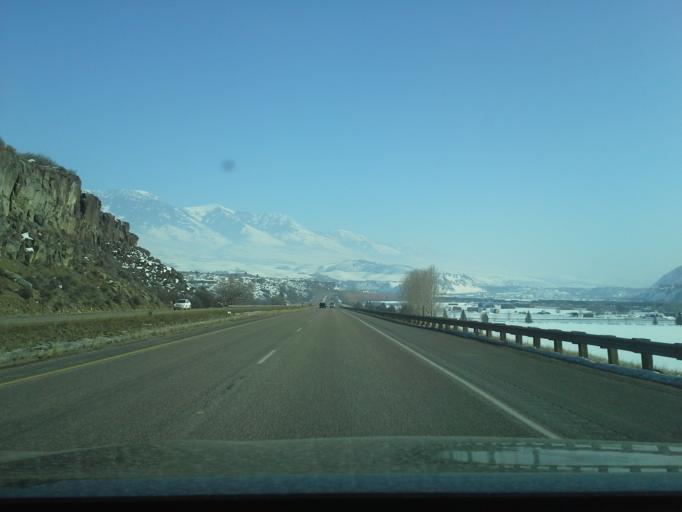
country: US
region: Idaho
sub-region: Bannock County
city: Pocatello
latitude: 42.7957
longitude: -112.2480
